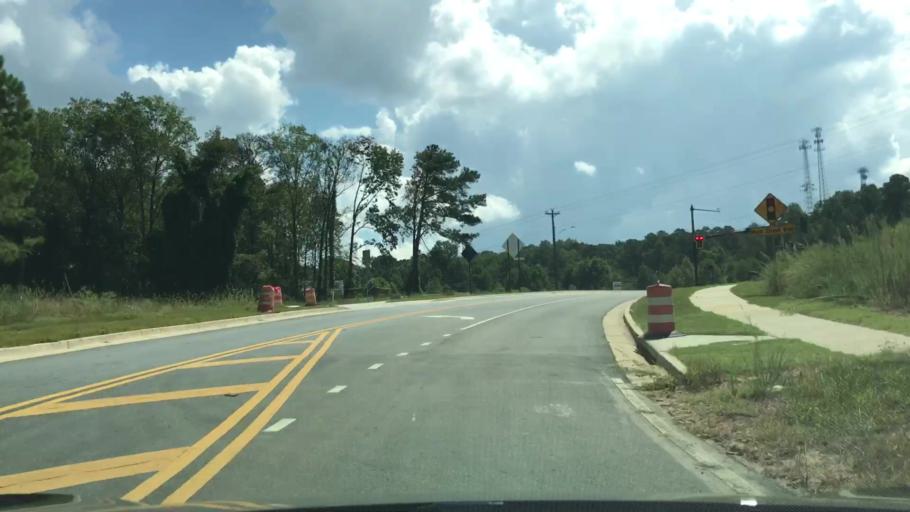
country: US
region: Georgia
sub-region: Gwinnett County
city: Snellville
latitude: 33.8535
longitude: -84.0402
